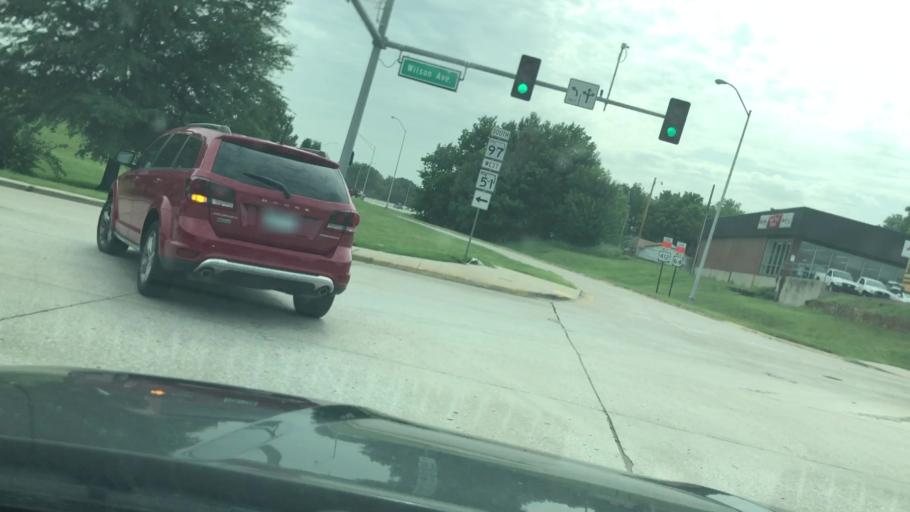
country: US
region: Oklahoma
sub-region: Tulsa County
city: Sand Springs
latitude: 36.1373
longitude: -96.1152
